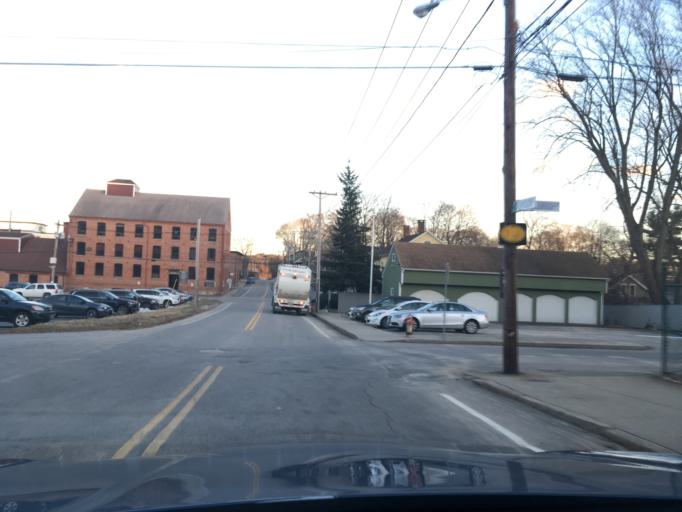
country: US
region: Rhode Island
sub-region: Kent County
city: East Greenwich
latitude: 41.6640
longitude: -71.4494
